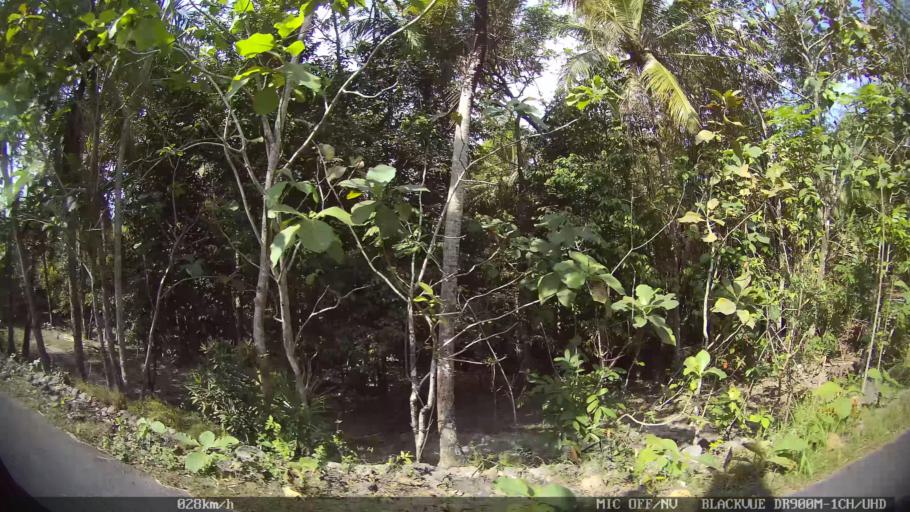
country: ID
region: Daerah Istimewa Yogyakarta
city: Kasihan
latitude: -7.8489
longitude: 110.3005
